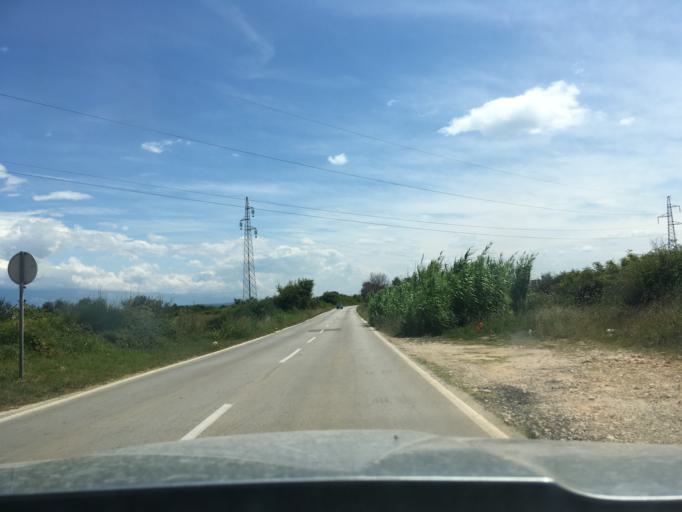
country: HR
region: Zadarska
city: Nin
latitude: 44.2464
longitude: 15.1619
